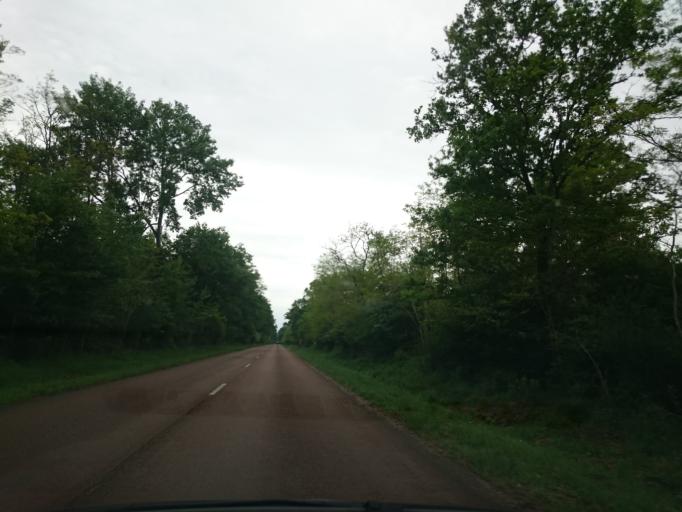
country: FR
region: Centre
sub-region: Departement du Loir-et-Cher
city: Muides-sur-Loire
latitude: 47.6431
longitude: 1.5241
